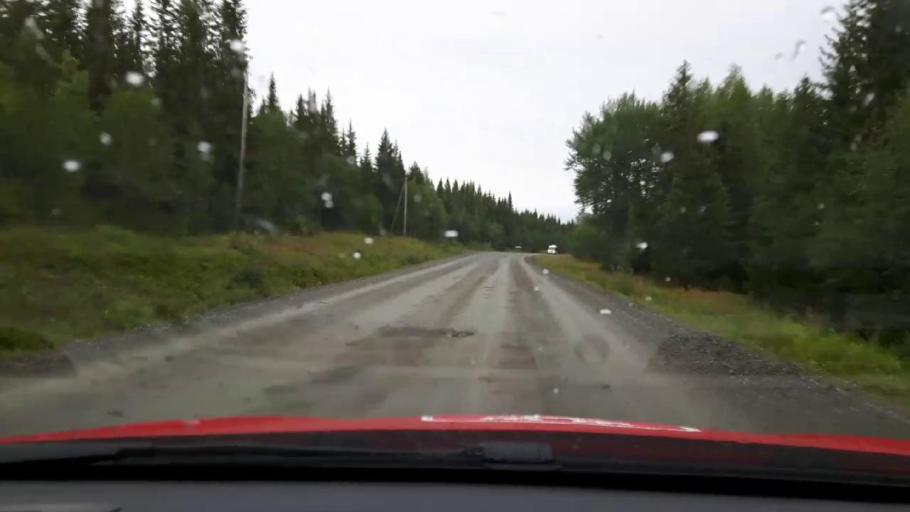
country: SE
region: Jaemtland
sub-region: Are Kommun
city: Are
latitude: 63.4539
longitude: 12.6478
